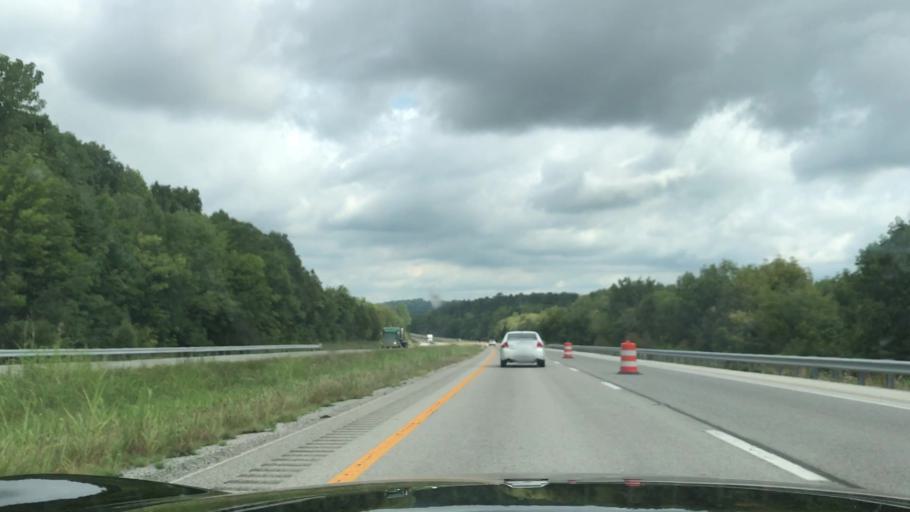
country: US
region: Kentucky
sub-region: Butler County
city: Morgantown
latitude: 37.1179
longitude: -86.6417
